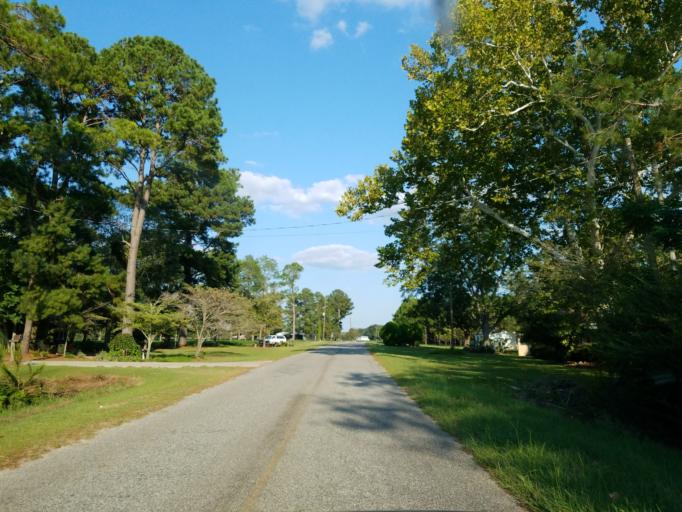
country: US
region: Georgia
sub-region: Cook County
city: Sparks
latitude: 31.2372
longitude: -83.4783
